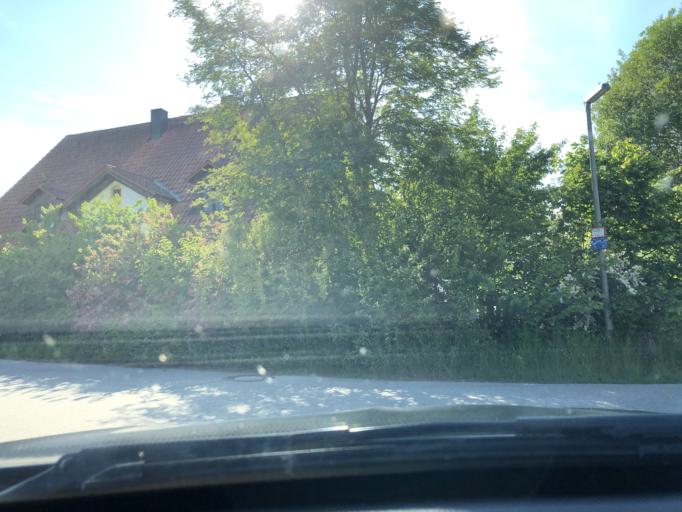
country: DE
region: Bavaria
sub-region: Upper Bavaria
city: Kirchdorf
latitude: 48.4387
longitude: 11.6815
